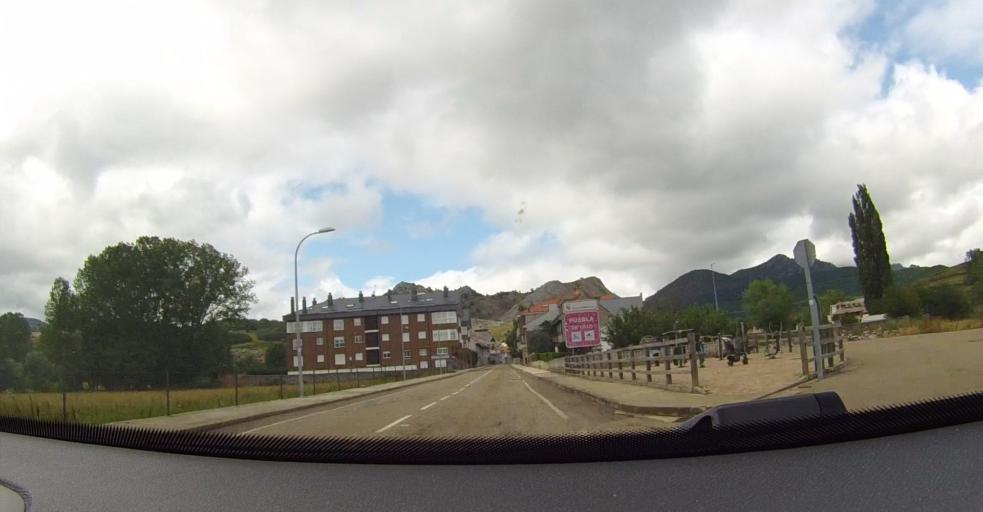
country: ES
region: Castille and Leon
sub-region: Provincia de Leon
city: Puebla de Lillo
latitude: 43.0055
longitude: -5.2712
